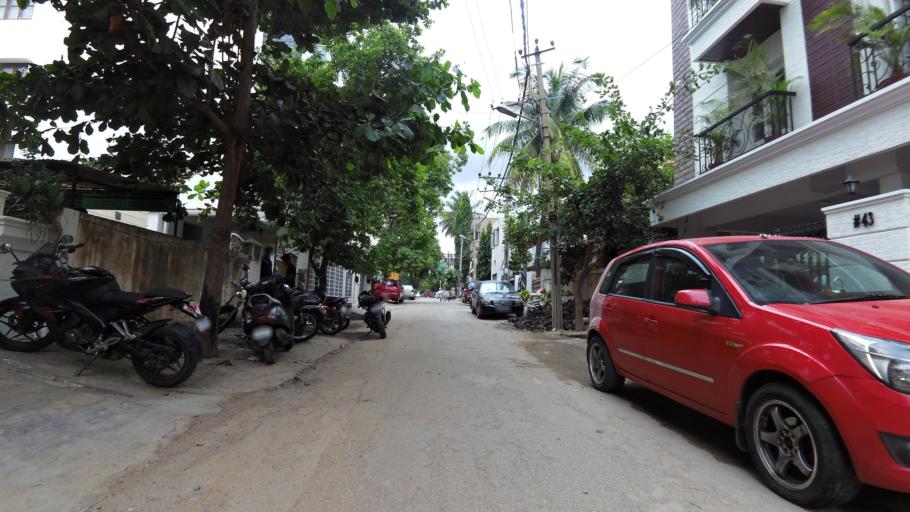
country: IN
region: Karnataka
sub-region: Bangalore Urban
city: Bangalore
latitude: 13.0045
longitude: 77.6270
